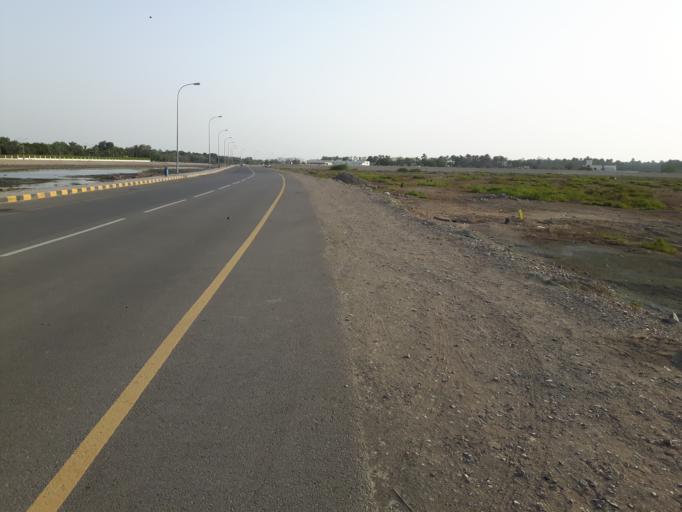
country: OM
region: Al Batinah
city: Al Sohar
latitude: 24.4063
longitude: 56.7129
